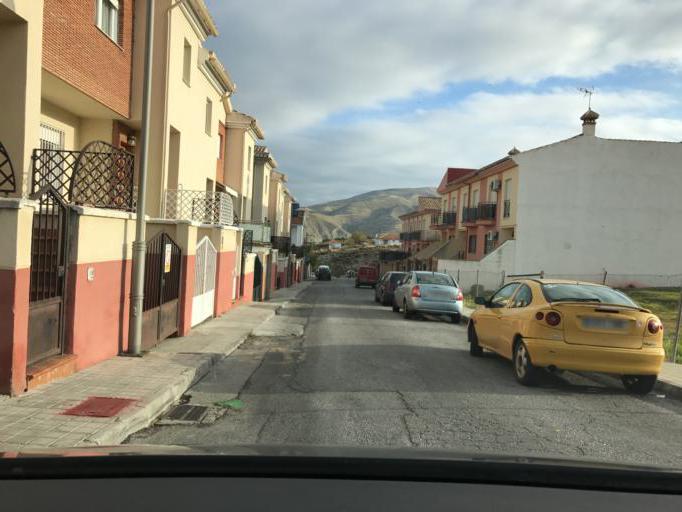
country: ES
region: Andalusia
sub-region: Provincia de Granada
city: Monachil
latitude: 37.1243
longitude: -3.5514
